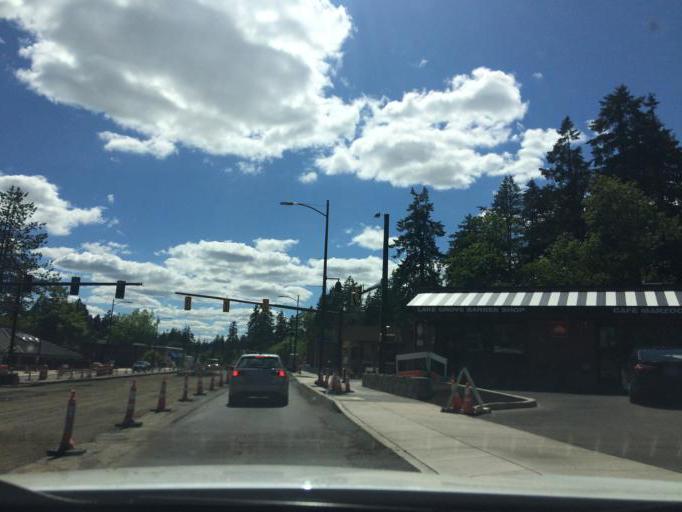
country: US
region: Oregon
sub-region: Washington County
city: Durham
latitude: 45.4099
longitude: -122.7206
